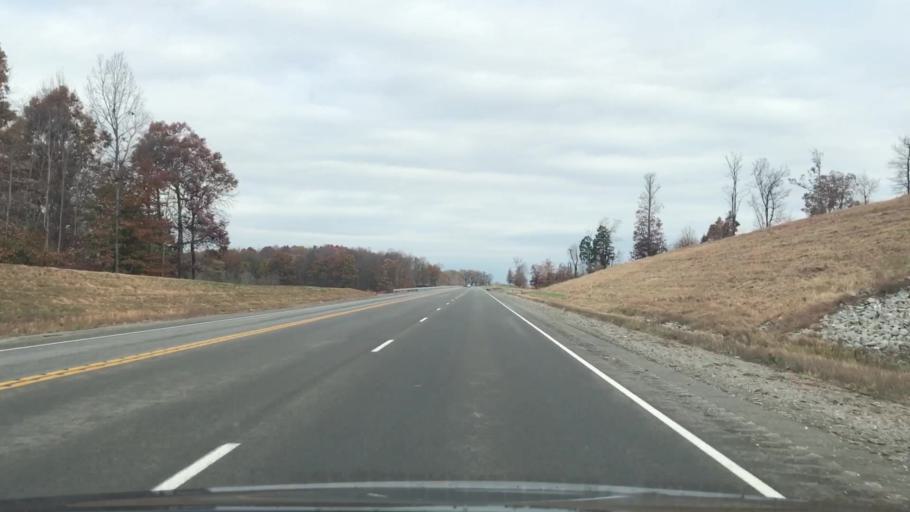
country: US
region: Kentucky
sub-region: Metcalfe County
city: Edmonton
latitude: 36.8509
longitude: -85.6746
